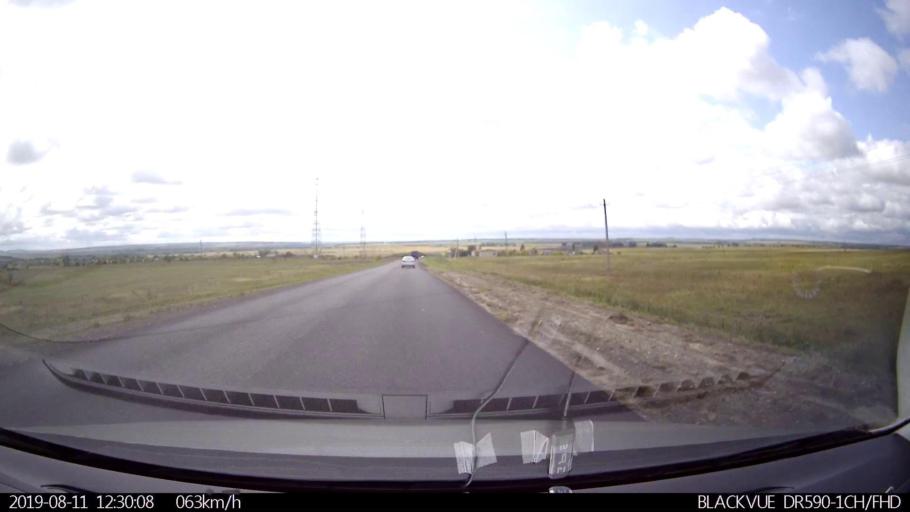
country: RU
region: Ulyanovsk
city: Ignatovka
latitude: 53.8284
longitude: 47.8966
